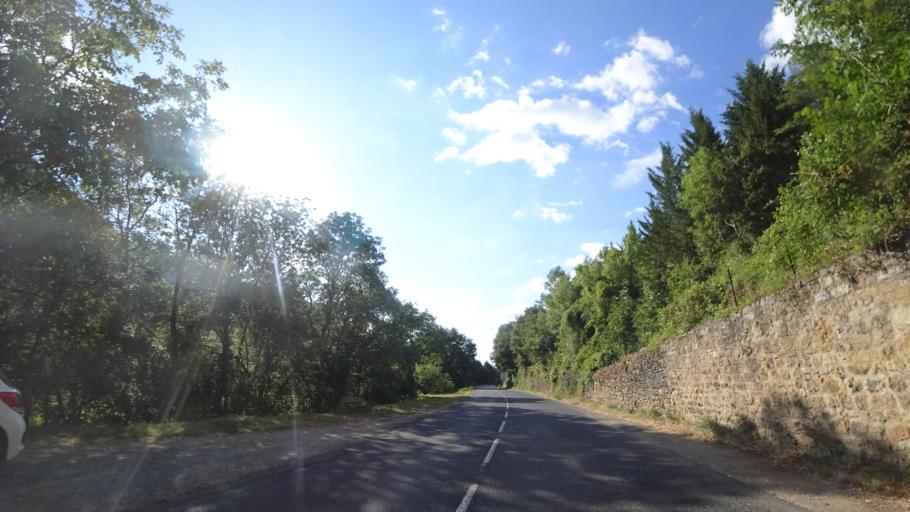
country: FR
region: Languedoc-Roussillon
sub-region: Departement de la Lozere
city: La Canourgue
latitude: 44.4184
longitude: 3.2303
